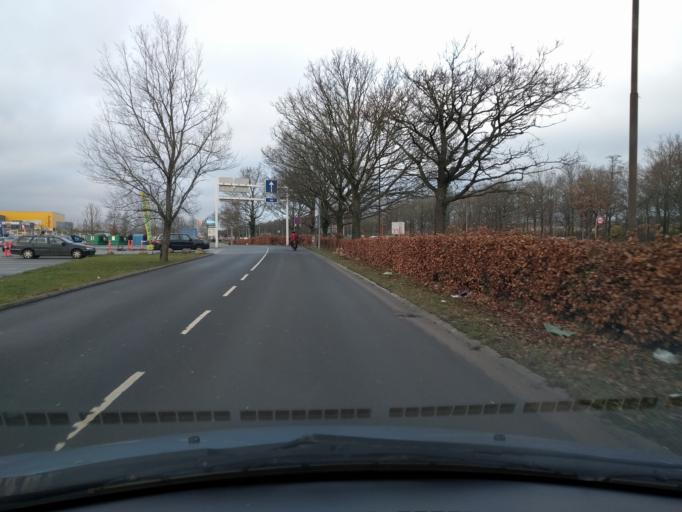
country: DK
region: South Denmark
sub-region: Odense Kommune
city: Neder Holluf
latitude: 55.3777
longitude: 10.4349
